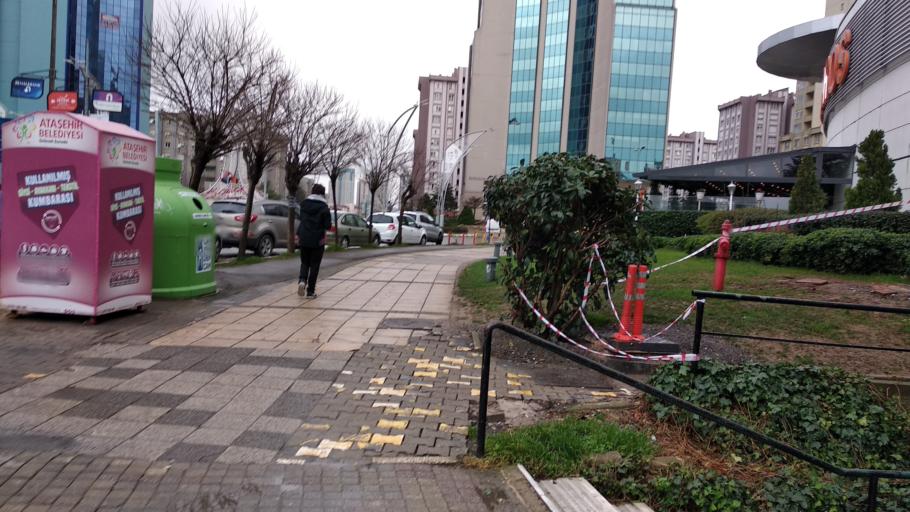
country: TR
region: Istanbul
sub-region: Atasehir
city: Atasehir
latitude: 40.9926
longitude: 29.1264
